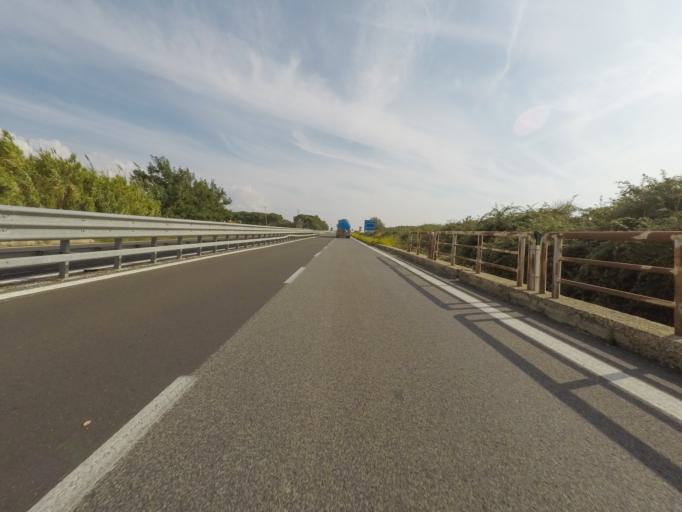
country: IT
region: Latium
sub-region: Provincia di Viterbo
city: Montalto di Castro
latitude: 42.3314
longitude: 11.6282
